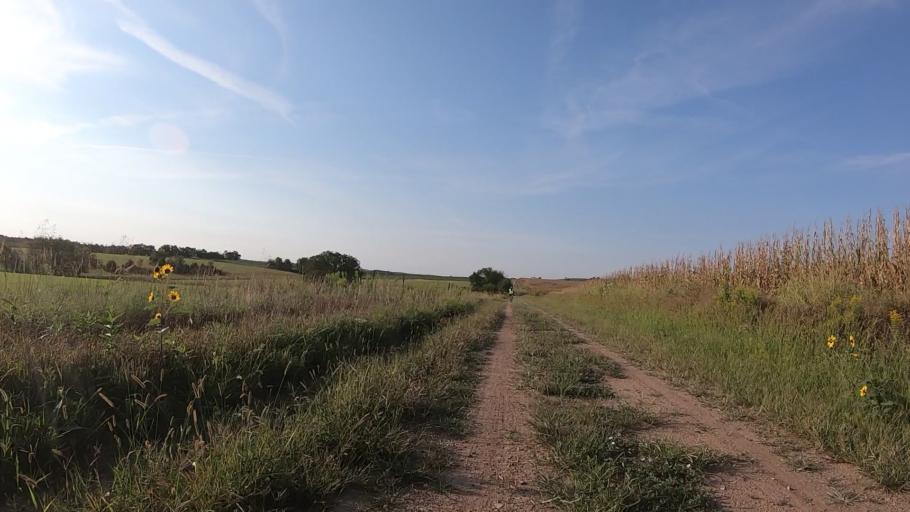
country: US
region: Kansas
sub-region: Marshall County
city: Blue Rapids
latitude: 39.7014
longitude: -96.7792
